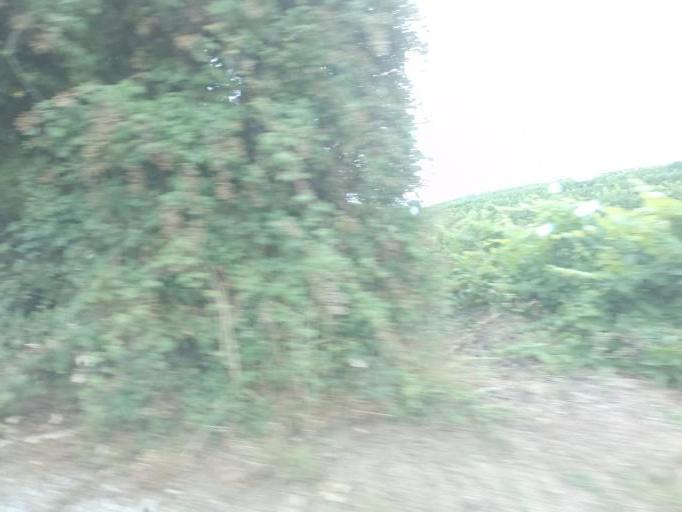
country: PT
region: Vila Real
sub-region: Sabrosa
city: Sabrosa
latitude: 41.2362
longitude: -7.4951
